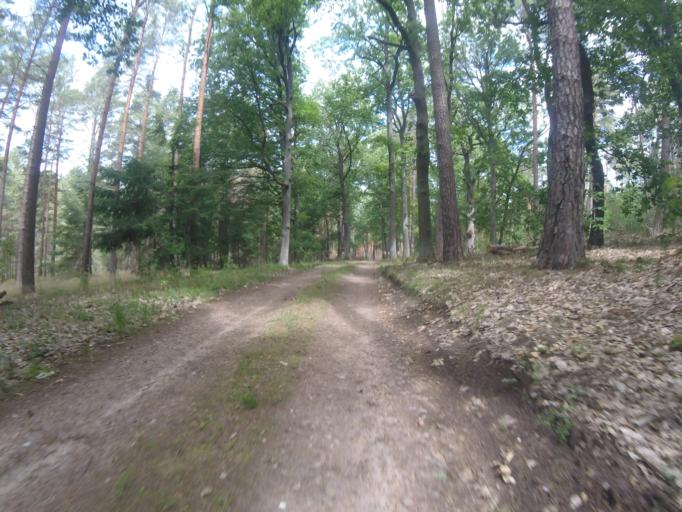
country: DE
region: Brandenburg
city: Gross Koris
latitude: 52.1991
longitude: 13.6744
